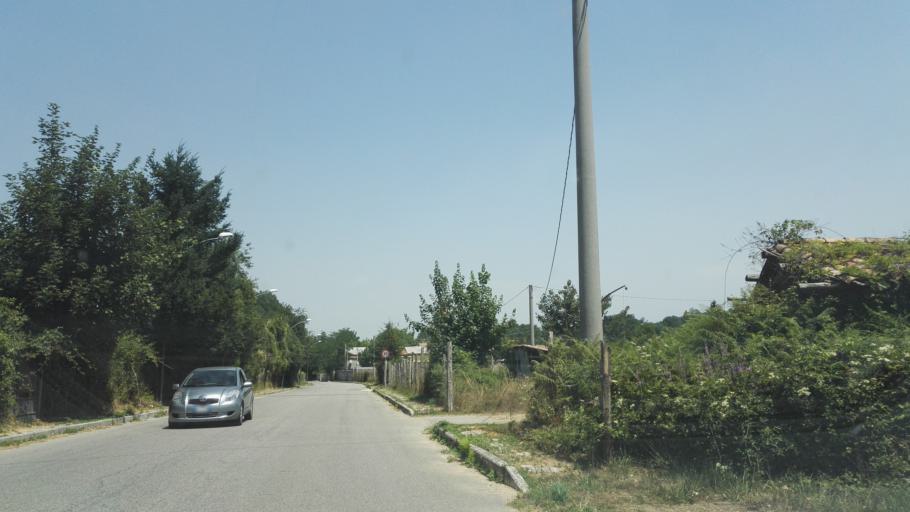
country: IT
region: Calabria
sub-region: Provincia di Vibo-Valentia
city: Serra San Bruno
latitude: 38.5737
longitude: 16.3309
